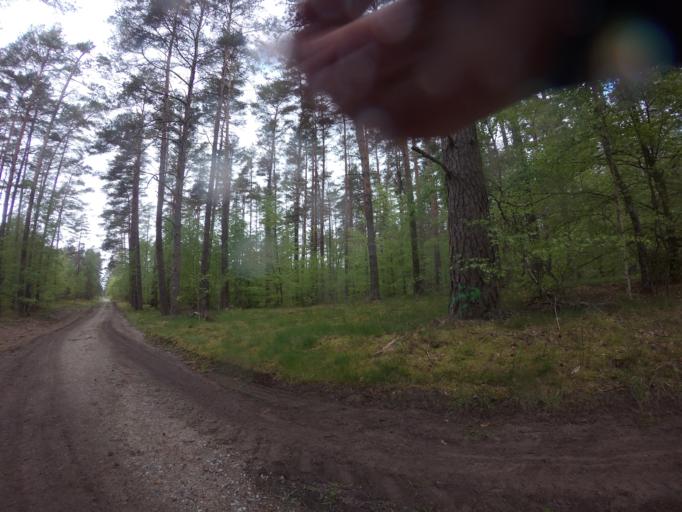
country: PL
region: West Pomeranian Voivodeship
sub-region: Powiat drawski
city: Kalisz Pomorski
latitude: 53.2239
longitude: 16.0139
